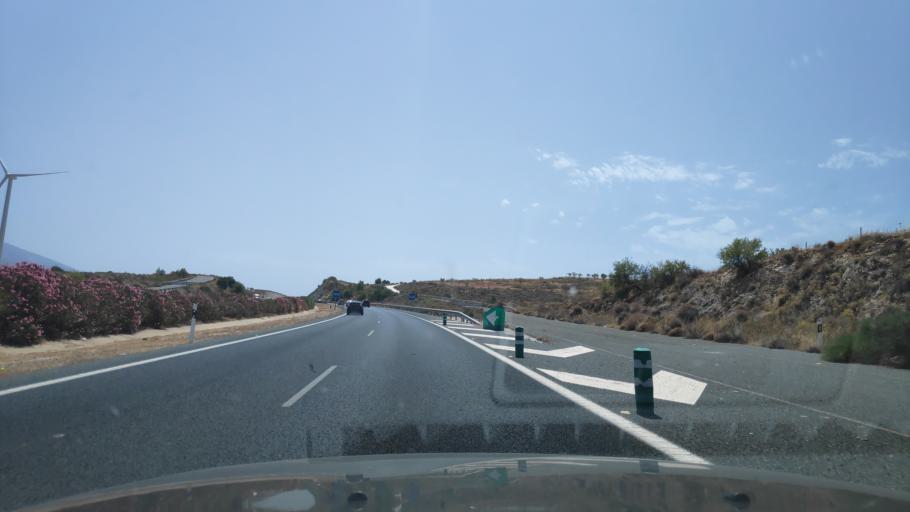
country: ES
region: Andalusia
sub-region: Provincia de Granada
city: Padul
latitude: 37.0060
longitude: -3.6381
